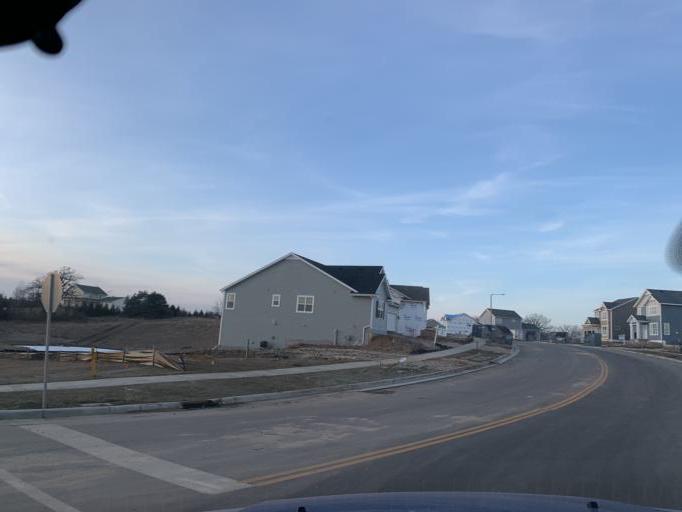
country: US
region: Wisconsin
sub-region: Dane County
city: Verona
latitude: 43.0458
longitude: -89.5571
